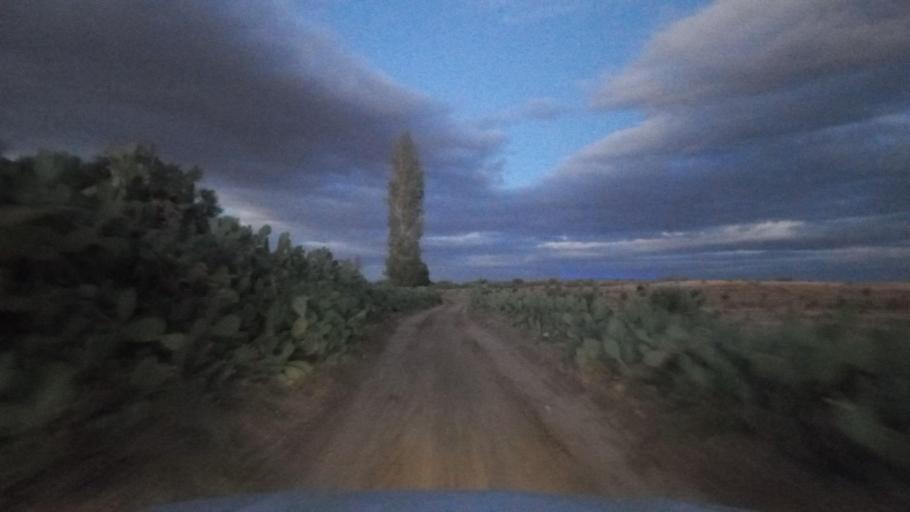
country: TN
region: Al Qasrayn
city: Kasserine
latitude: 35.2553
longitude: 8.9387
